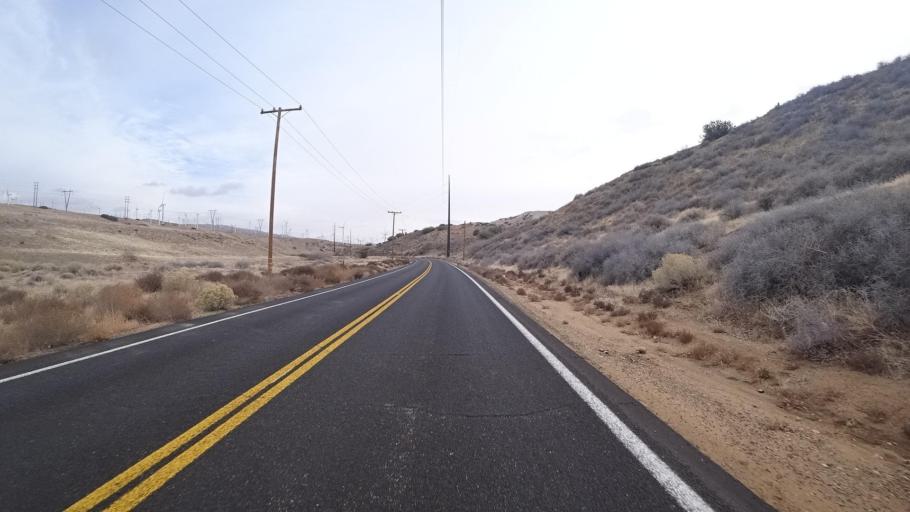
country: US
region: California
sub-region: Kern County
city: Tehachapi
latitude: 35.0501
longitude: -118.3514
